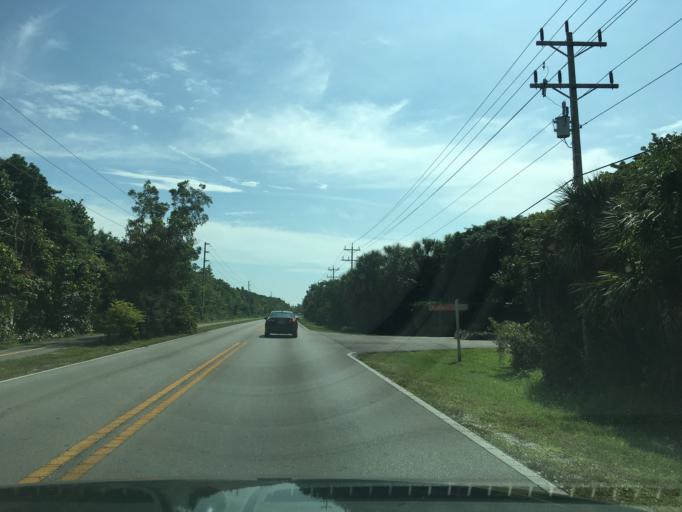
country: US
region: Florida
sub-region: Lee County
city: Saint James City
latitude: 26.4617
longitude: -82.1477
